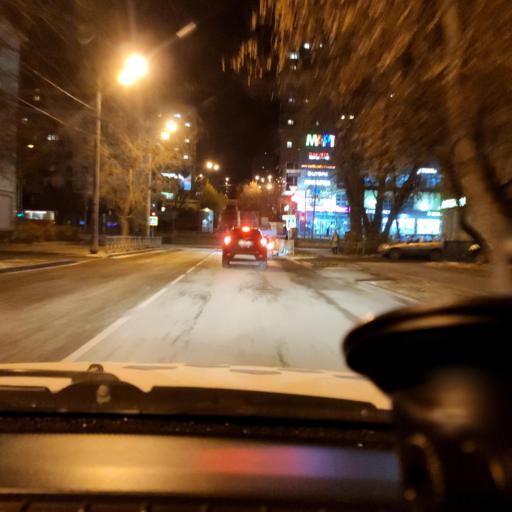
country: RU
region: Perm
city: Perm
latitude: 58.0066
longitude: 56.2054
